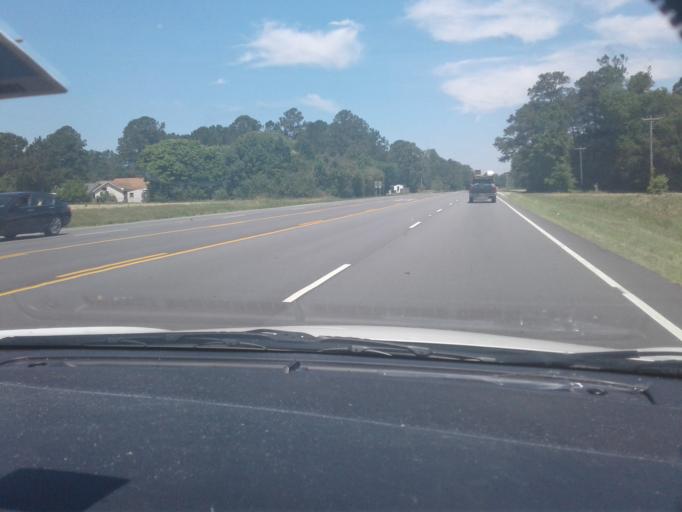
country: US
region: North Carolina
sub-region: Harnett County
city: Buies Creek
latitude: 35.3914
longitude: -78.7280
